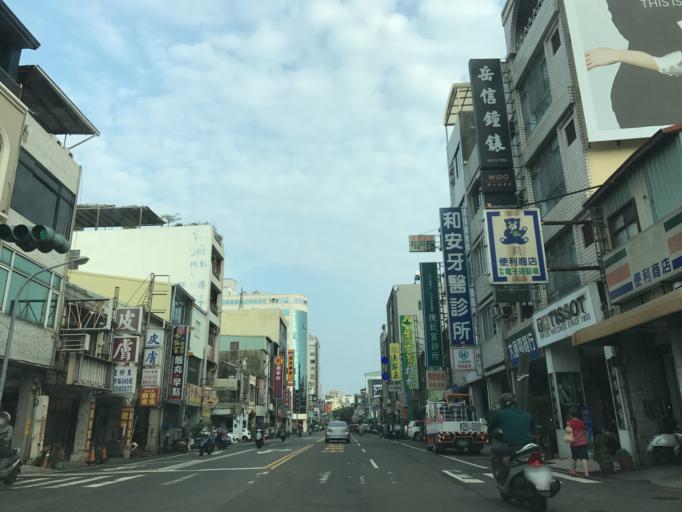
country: TW
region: Taiwan
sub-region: Tainan
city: Tainan
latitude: 22.9987
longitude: 120.1964
